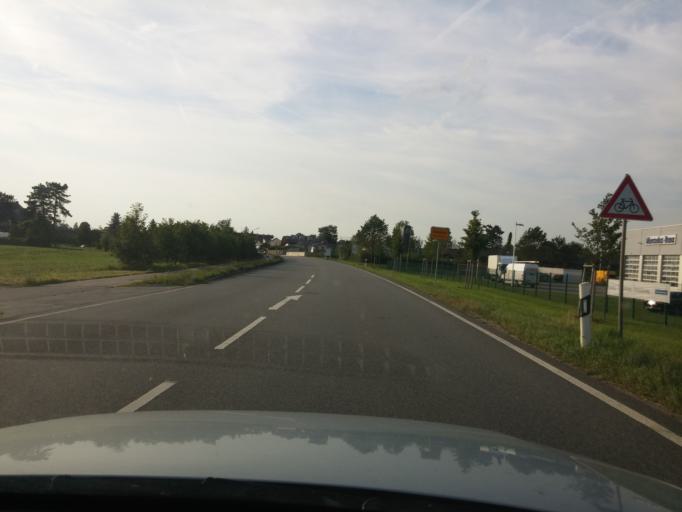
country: DE
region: Bavaria
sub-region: Upper Bavaria
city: Feldkirchen
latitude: 48.1412
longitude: 11.7355
